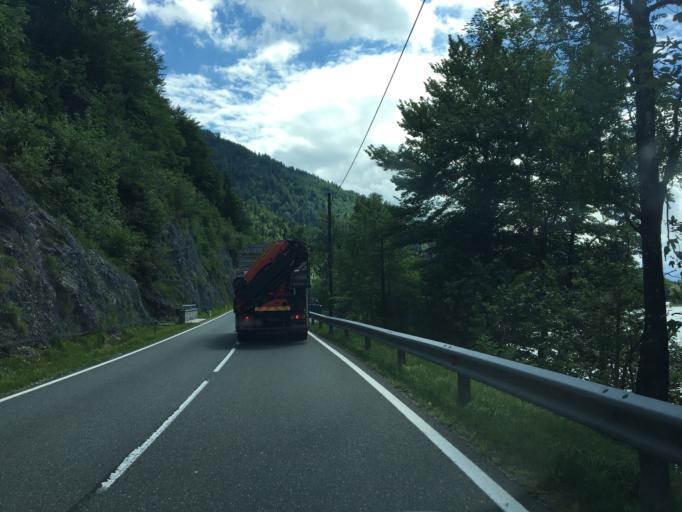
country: AT
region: Salzburg
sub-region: Politischer Bezirk Hallein
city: Krispl
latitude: 47.7491
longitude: 13.1733
